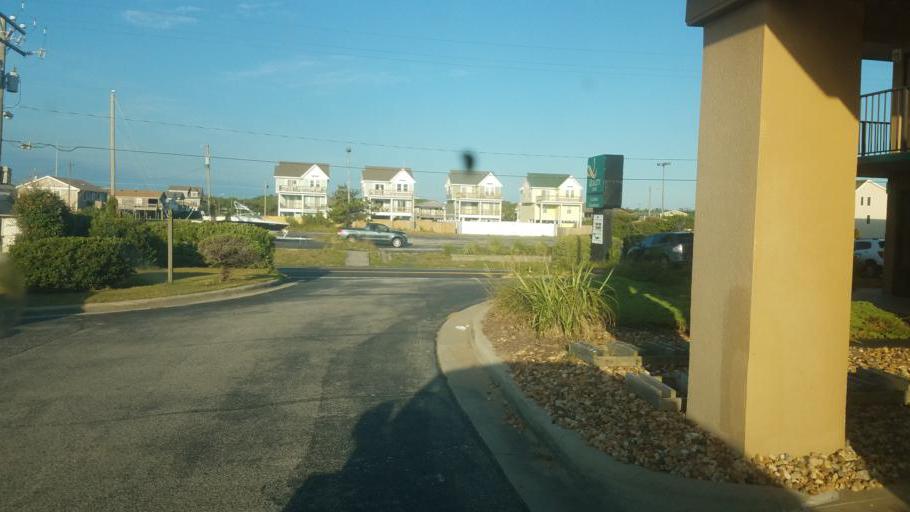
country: US
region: North Carolina
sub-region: Dare County
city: Kill Devil Hills
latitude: 36.0170
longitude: -75.6585
